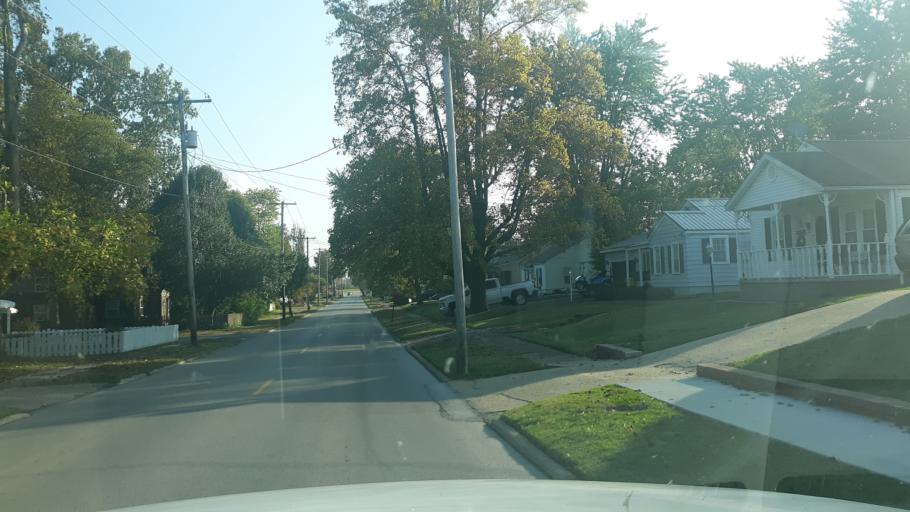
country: US
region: Illinois
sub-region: Saline County
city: Harrisburg
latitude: 37.7271
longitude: -88.5403
